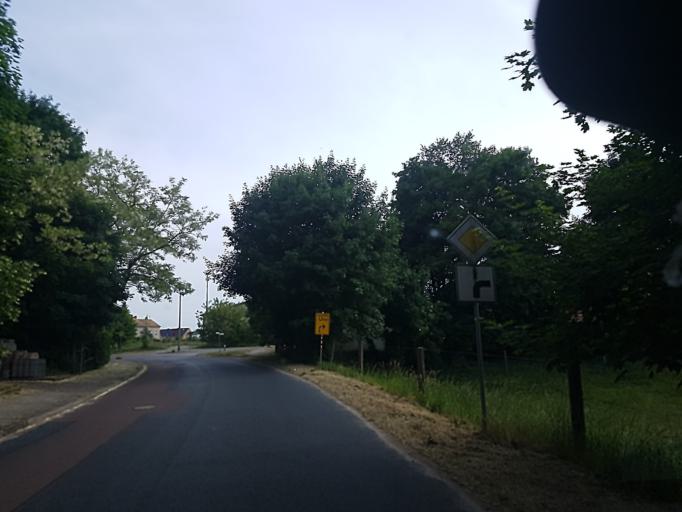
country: DE
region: Saxony-Anhalt
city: Zahna
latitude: 51.9220
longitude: 12.7807
